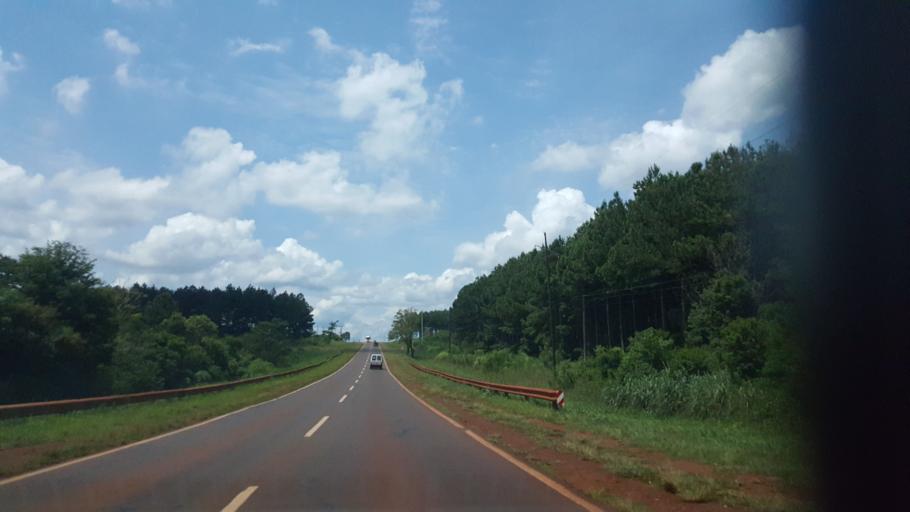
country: AR
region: Misiones
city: Puerto Rico
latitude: -26.8208
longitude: -55.0063
